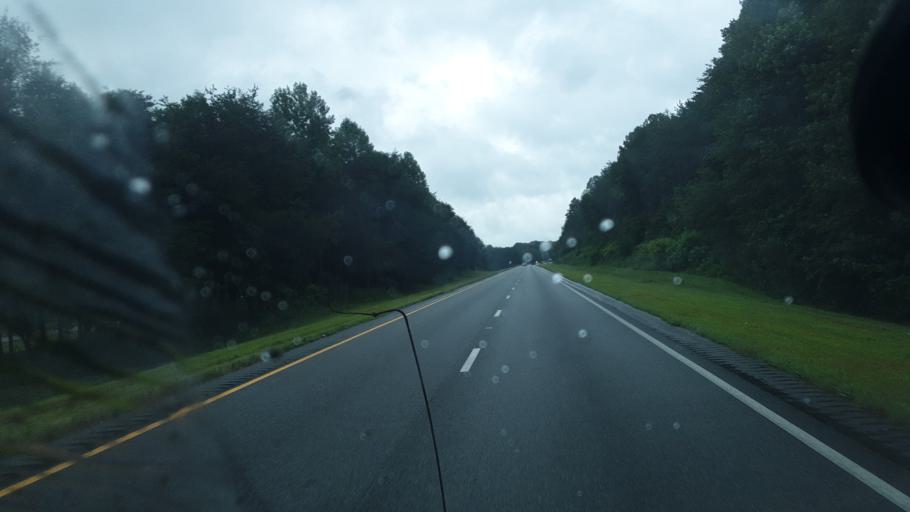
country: US
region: North Carolina
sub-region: Davidson County
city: Wallburg
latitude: 36.0547
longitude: -80.1484
